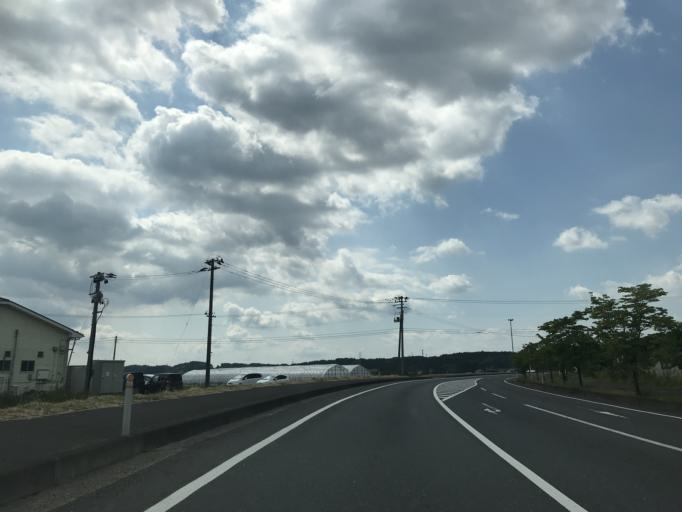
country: JP
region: Miyagi
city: Furukawa
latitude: 38.7410
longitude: 140.9595
